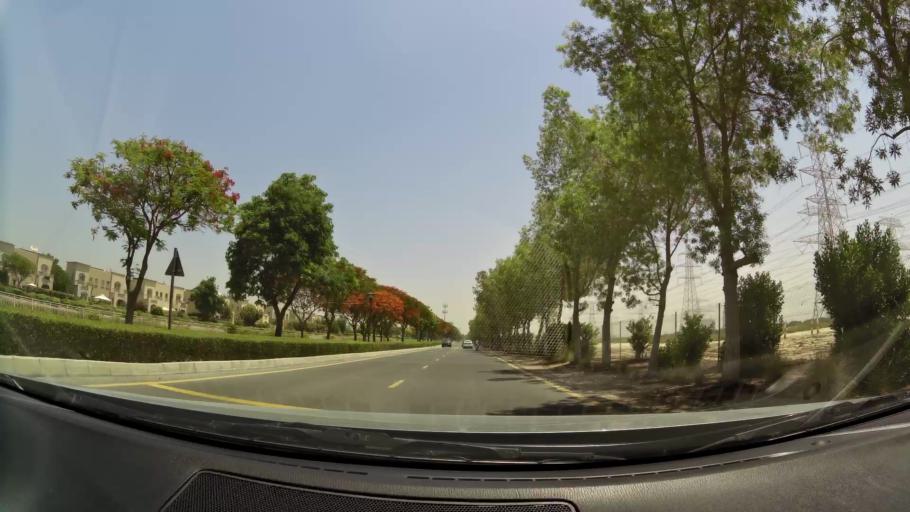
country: AE
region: Dubai
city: Dubai
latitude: 25.0483
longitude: 55.1798
